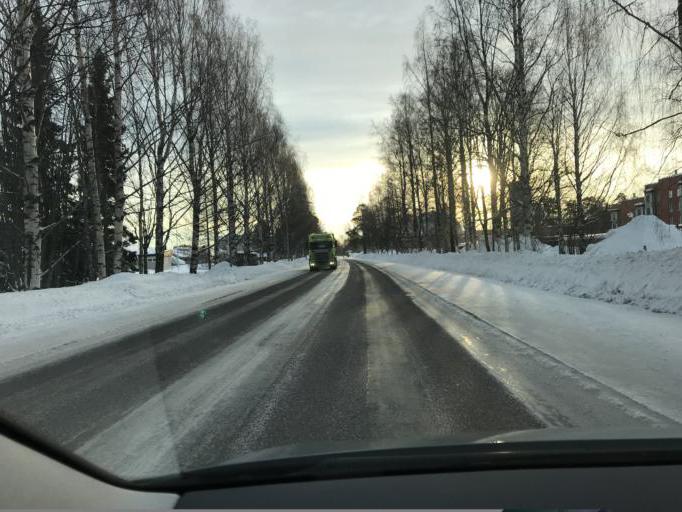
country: SE
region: Norrbotten
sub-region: Lulea Kommun
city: Bergnaset
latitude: 65.6050
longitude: 22.1150
